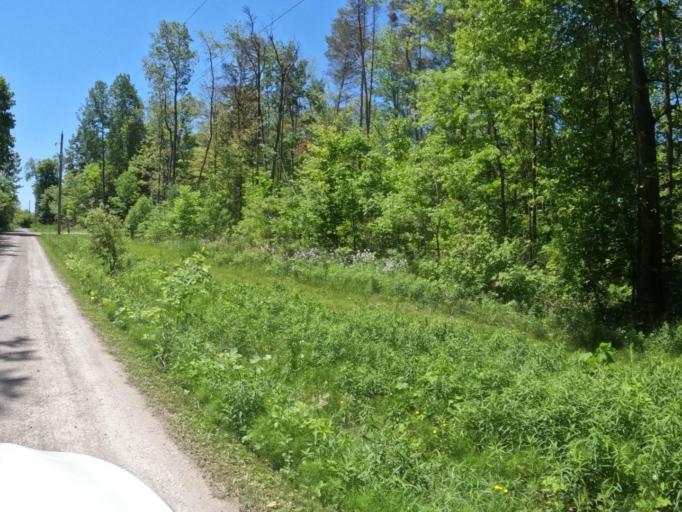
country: CA
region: Ontario
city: Norfolk County
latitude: 42.7802
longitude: -80.2309
